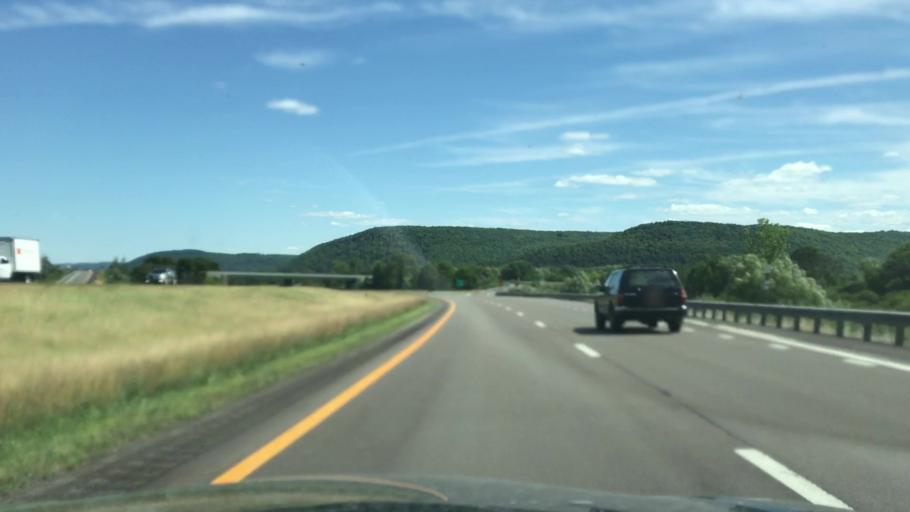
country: US
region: New York
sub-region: Steuben County
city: Bath
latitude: 42.4044
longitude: -77.4087
